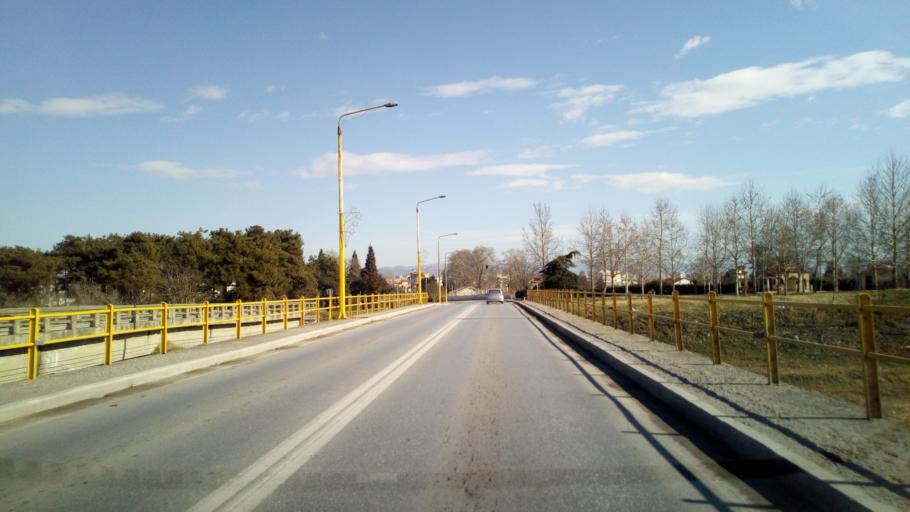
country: GR
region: Central Macedonia
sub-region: Nomos Thessalonikis
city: Lagkadas
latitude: 40.7449
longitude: 23.0587
